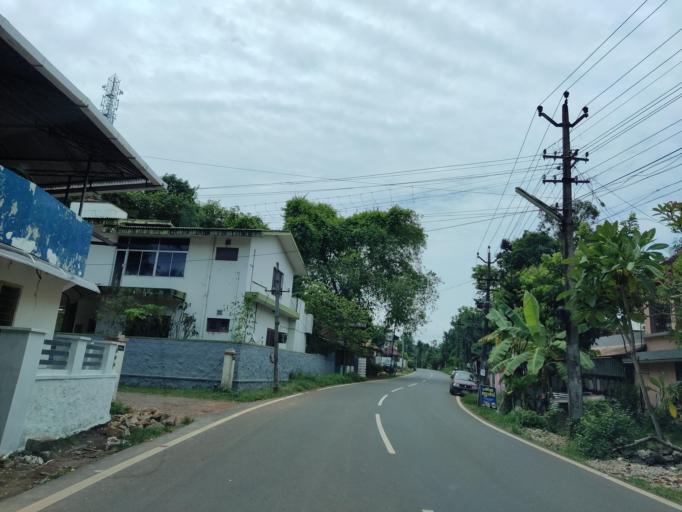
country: IN
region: Kerala
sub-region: Alappuzha
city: Chengannur
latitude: 9.2882
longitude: 76.6172
